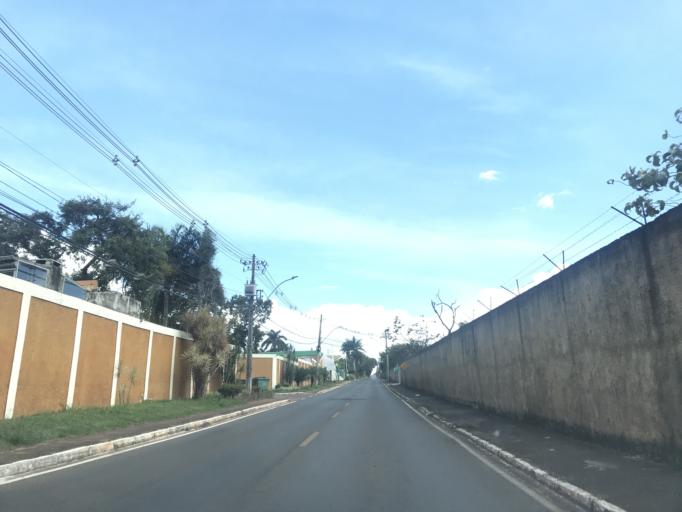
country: BR
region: Federal District
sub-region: Brasilia
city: Brasilia
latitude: -15.8796
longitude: -47.8116
